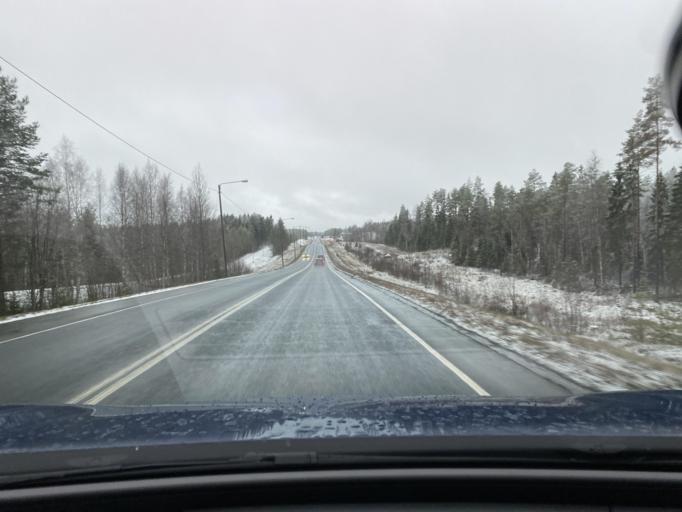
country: FI
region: Northern Ostrobothnia
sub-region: Oulu
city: Kiiminki
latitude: 65.1221
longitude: 25.7531
